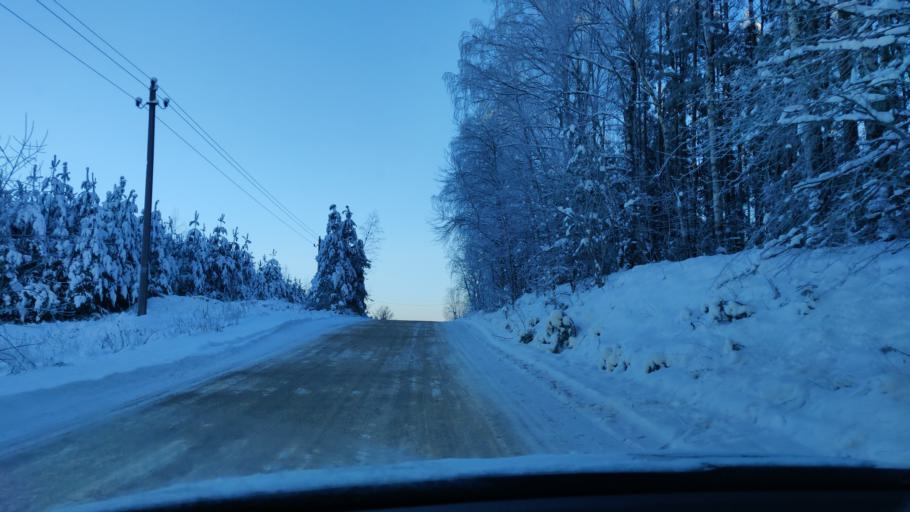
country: LT
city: Trakai
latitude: 54.6151
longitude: 24.9544
